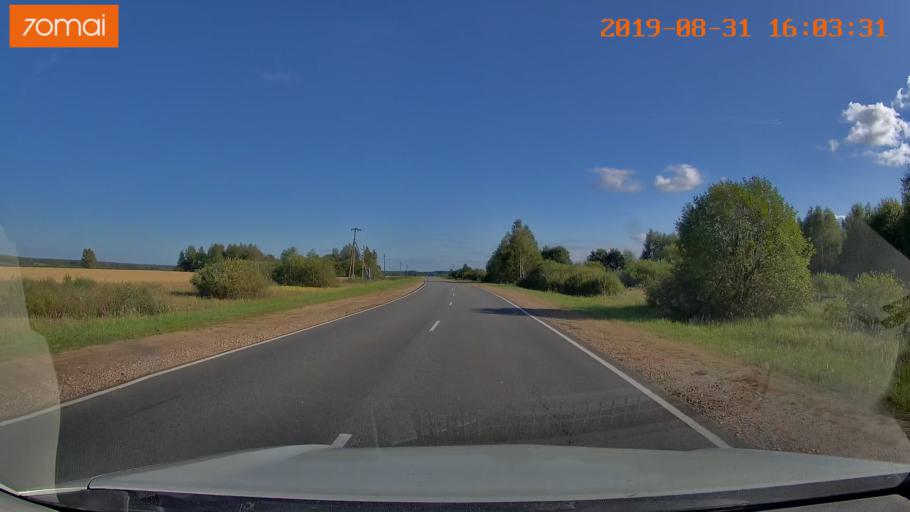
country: RU
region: Kaluga
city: Yukhnov
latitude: 54.6643
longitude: 35.3137
